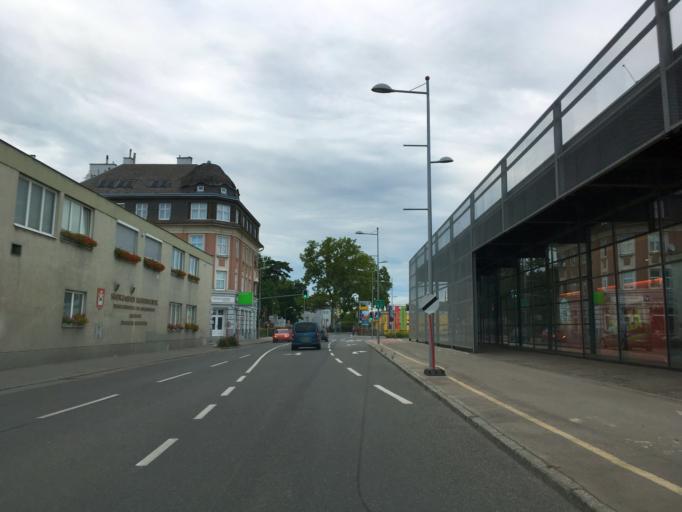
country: AT
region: Lower Austria
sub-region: Politischer Bezirk Wien-Umgebung
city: Klosterneuburg
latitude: 48.2989
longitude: 16.3333
